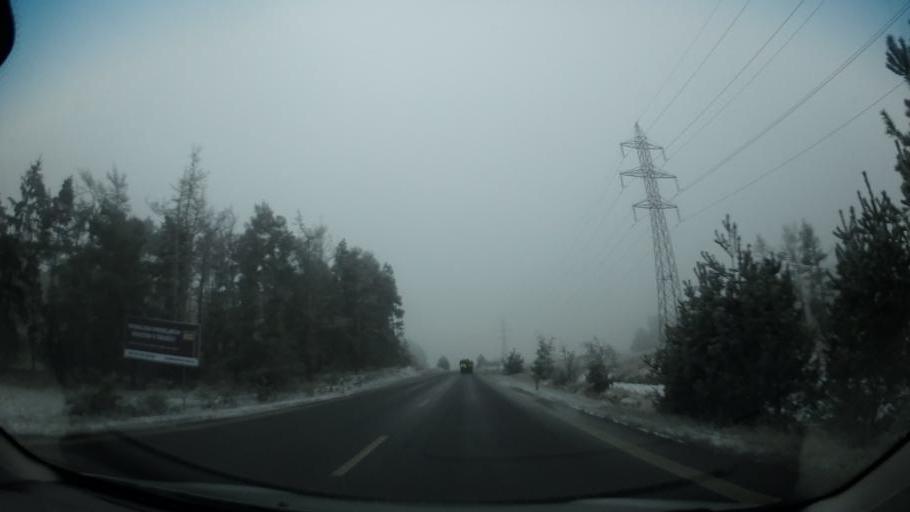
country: CZ
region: Vysocina
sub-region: Okres Trebic
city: Trebic
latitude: 49.2549
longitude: 15.9135
